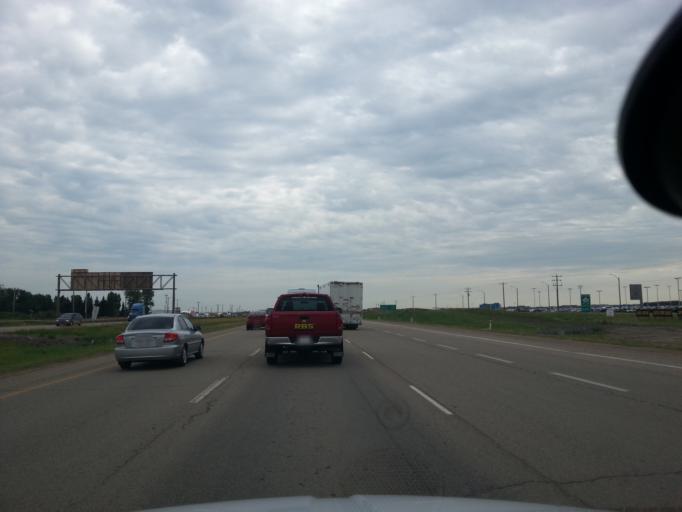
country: CA
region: Alberta
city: Sherwood Park
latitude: 53.5700
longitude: -113.3124
